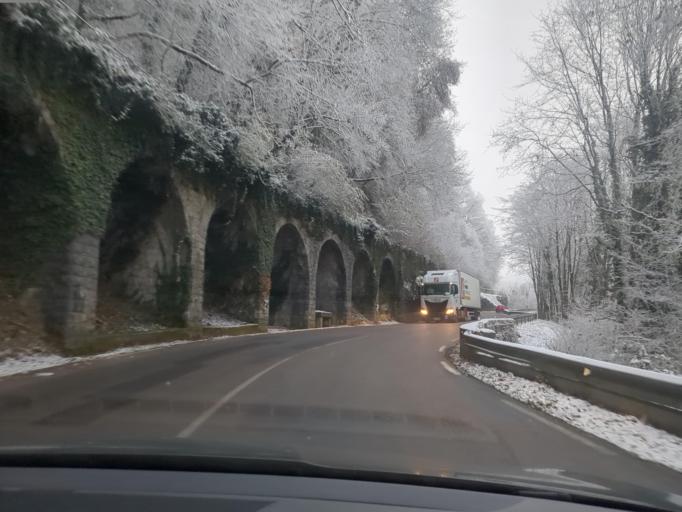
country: FR
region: Franche-Comte
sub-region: Departement du Jura
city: Perrigny
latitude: 46.6259
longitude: 5.6122
